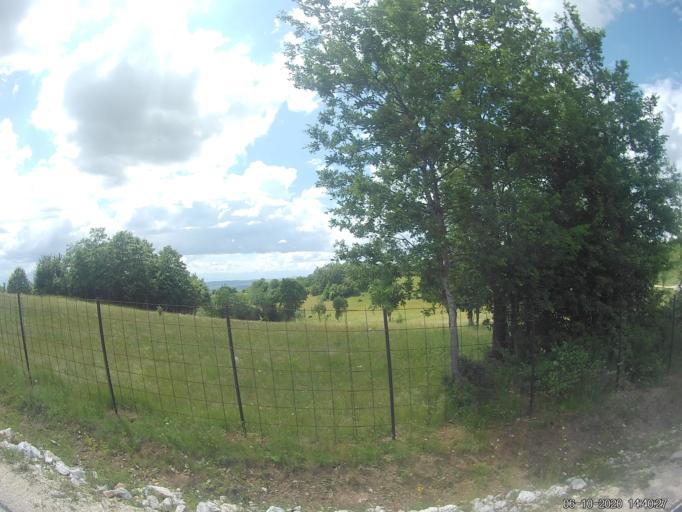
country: XK
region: Prizren
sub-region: Komuna e Therandes
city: Budakovo
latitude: 42.3961
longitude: 20.9434
